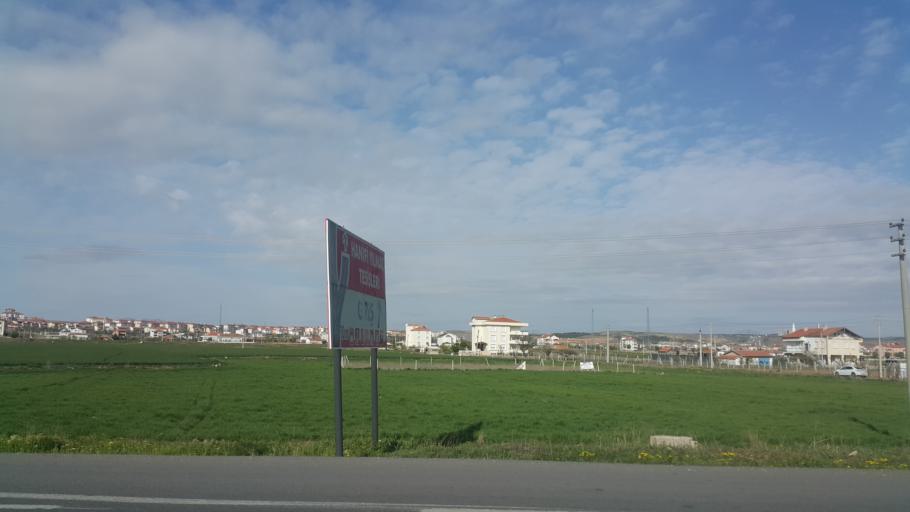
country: TR
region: Aksaray
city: Aksaray
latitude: 38.3997
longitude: 33.9836
